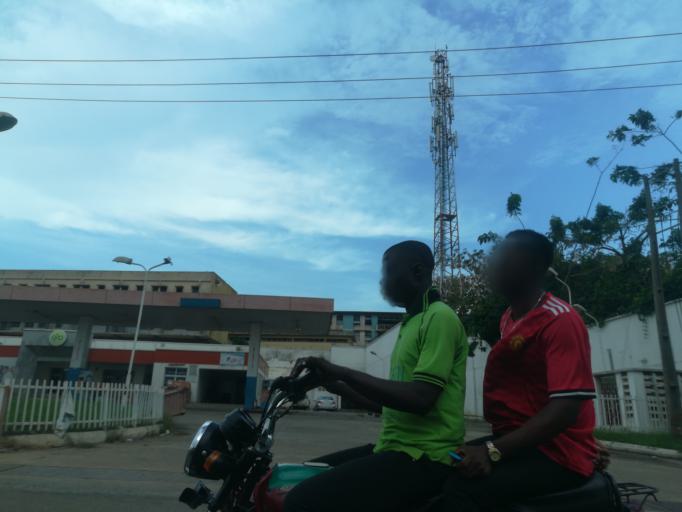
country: NG
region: Oyo
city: Ibadan
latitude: 7.4280
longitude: 3.8938
